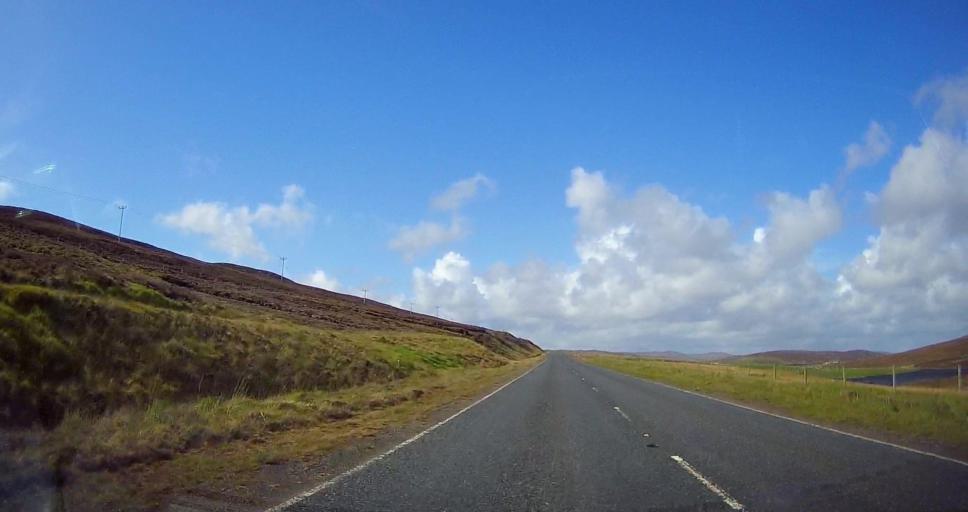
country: GB
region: Scotland
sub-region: Shetland Islands
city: Lerwick
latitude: 60.2133
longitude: -1.2337
